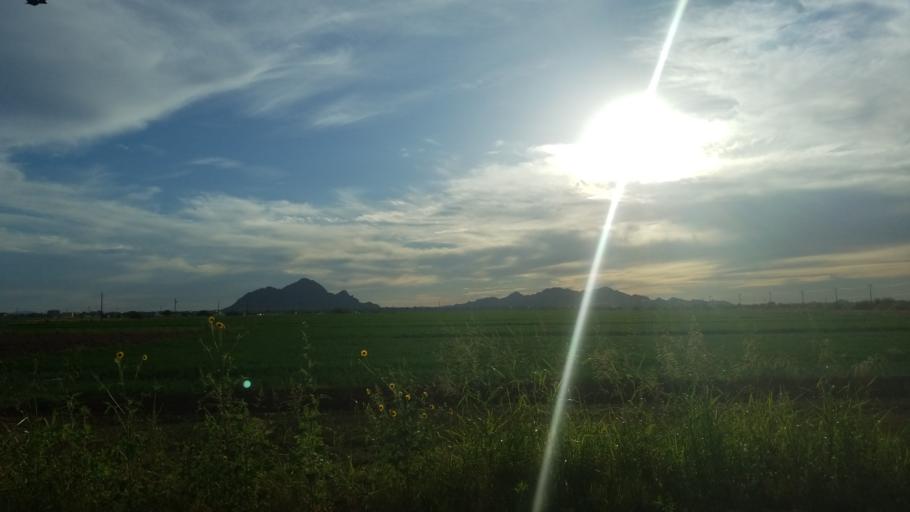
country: US
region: Arizona
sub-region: Maricopa County
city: Scottsdale
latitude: 33.5250
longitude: -111.8654
